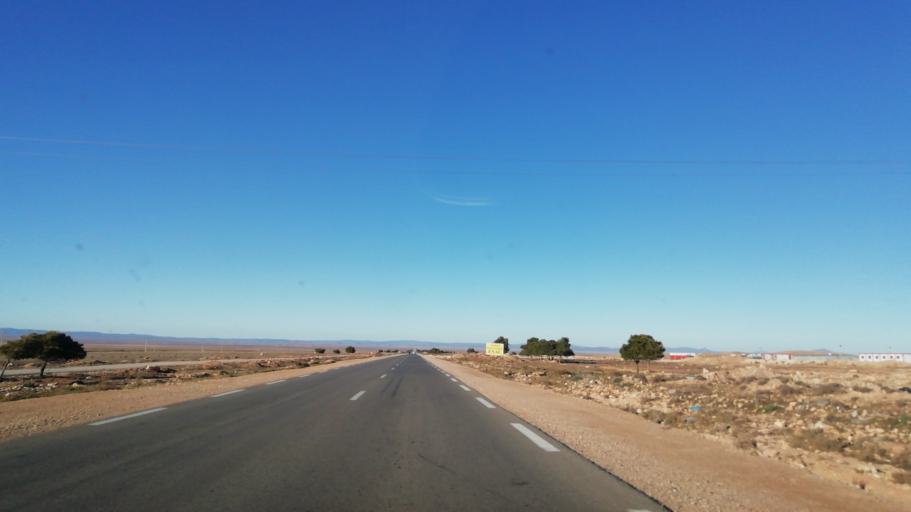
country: DZ
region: Tlemcen
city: Sebdou
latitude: 34.2988
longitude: -1.2610
